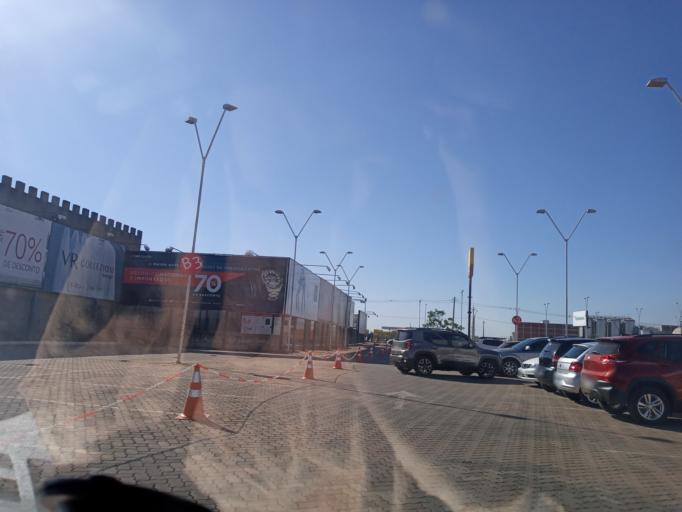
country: BR
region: Goias
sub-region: Abadiania
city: Abadiania
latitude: -16.1204
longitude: -48.3994
